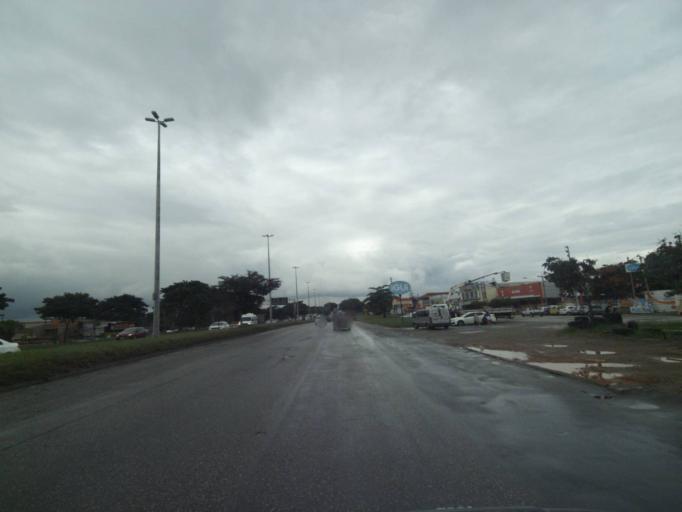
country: BR
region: Rio de Janeiro
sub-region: Nilopolis
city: Nilopolis
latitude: -22.8600
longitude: -43.4573
